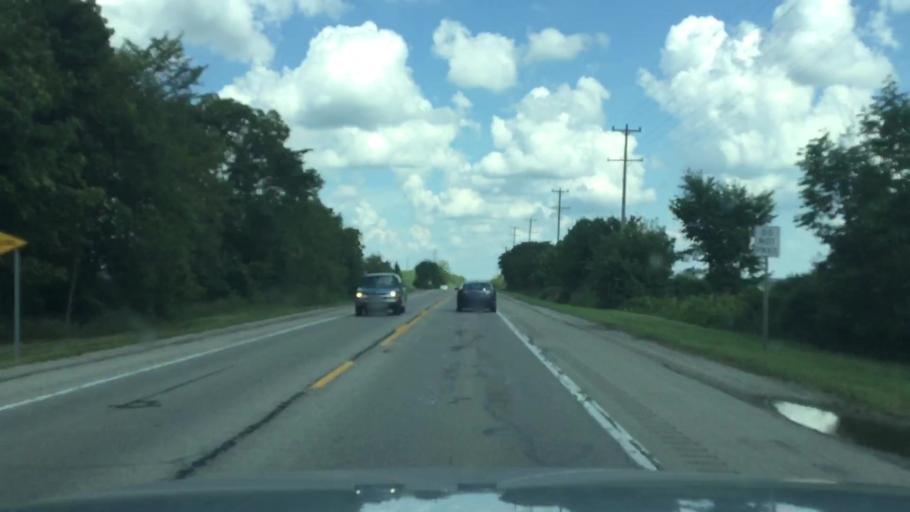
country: US
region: Michigan
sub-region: Washtenaw County
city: Saline
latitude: 42.1517
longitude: -83.8177
